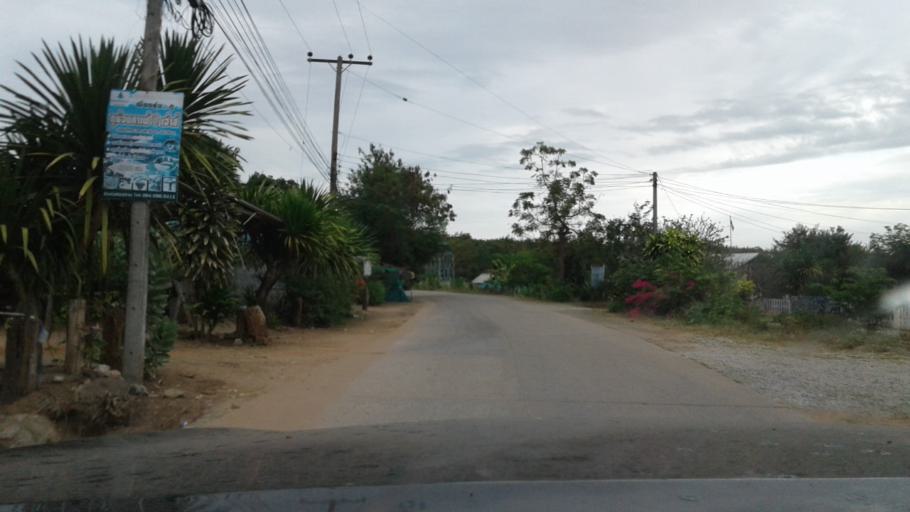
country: TH
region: Changwat Udon Thani
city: Nong Wua So
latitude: 17.2360
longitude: 102.5331
